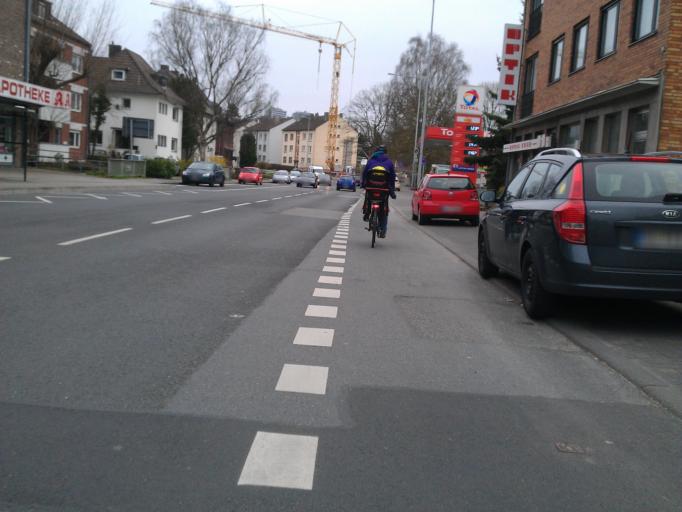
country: DE
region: North Rhine-Westphalia
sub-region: Regierungsbezirk Koln
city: Aachen
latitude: 50.7968
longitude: 6.0634
